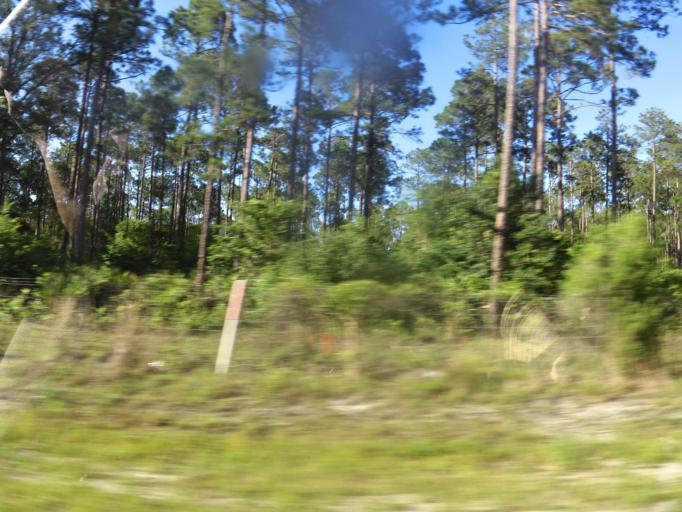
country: US
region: Florida
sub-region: Duval County
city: Jacksonville
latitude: 30.4633
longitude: -81.5443
